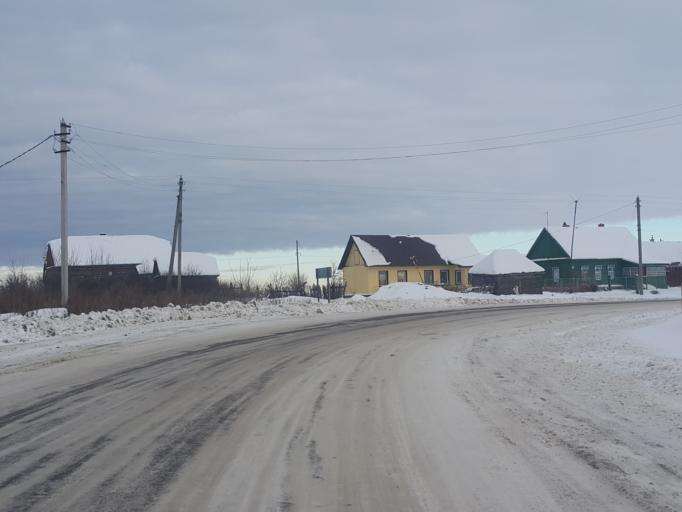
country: RU
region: Tambov
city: Platonovka
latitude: 52.8517
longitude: 41.8116
